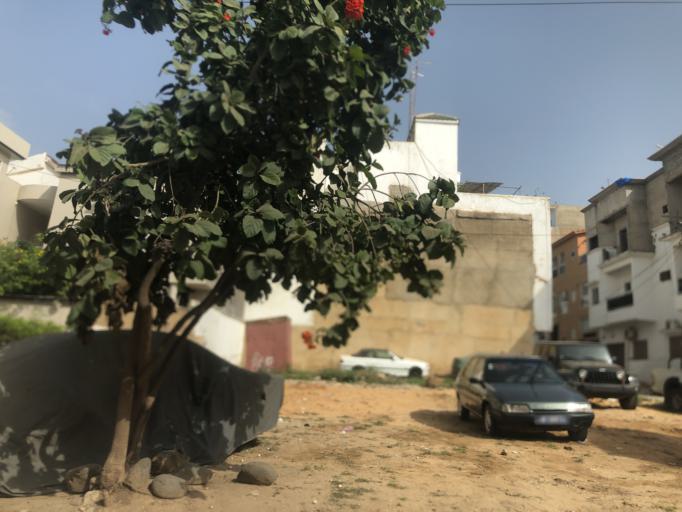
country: SN
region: Dakar
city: Mermoz Boabab
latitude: 14.7295
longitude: -17.4995
